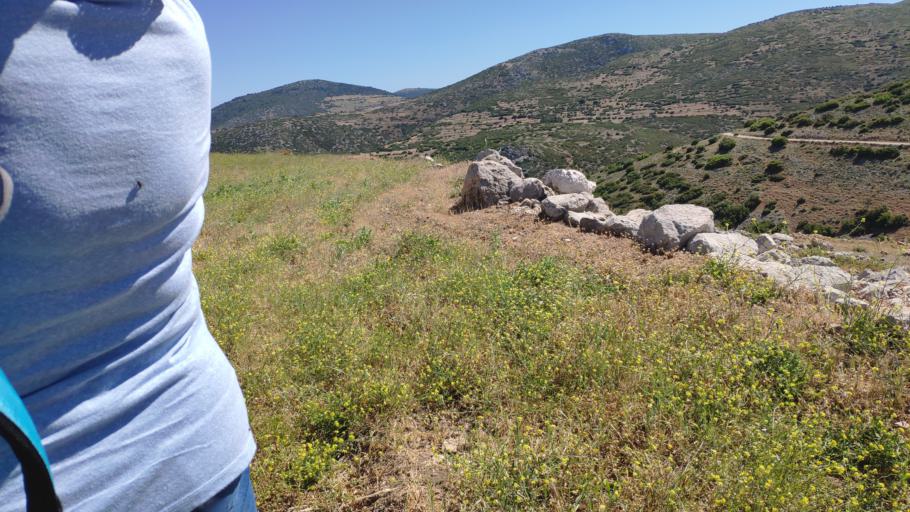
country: GR
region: Peloponnese
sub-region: Nomos Korinthias
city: Khiliomodhi
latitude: 37.7558
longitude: 22.8808
